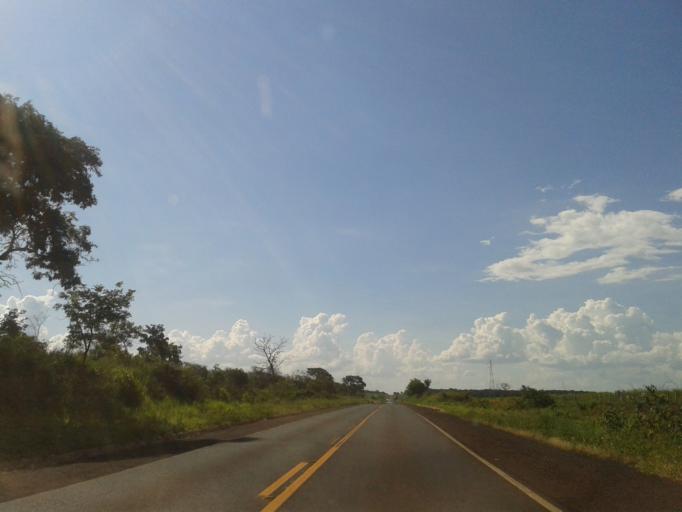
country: BR
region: Minas Gerais
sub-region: Santa Vitoria
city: Santa Vitoria
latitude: -19.0606
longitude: -50.3867
